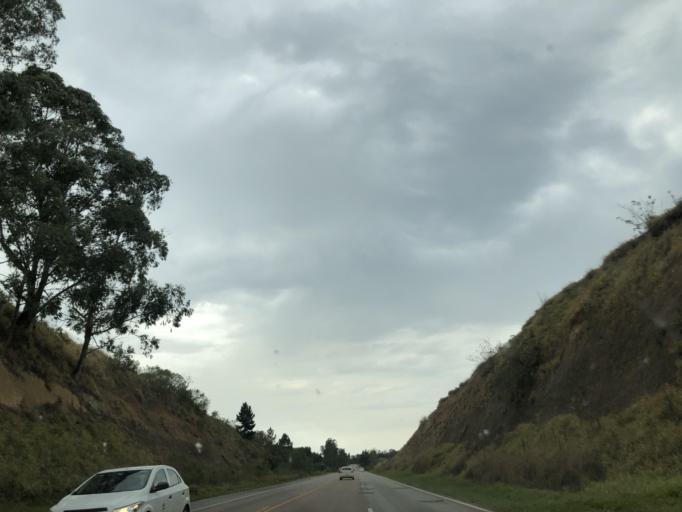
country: BR
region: Sao Paulo
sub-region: Salto De Pirapora
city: Salto de Pirapora
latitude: -23.7000
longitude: -47.6197
